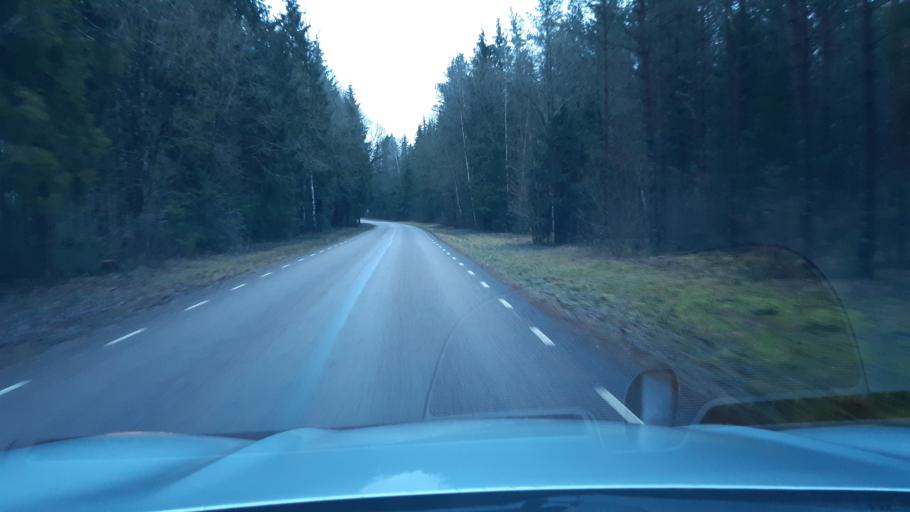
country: EE
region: Raplamaa
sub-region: Rapla vald
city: Rapla
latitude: 59.0219
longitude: 24.6867
